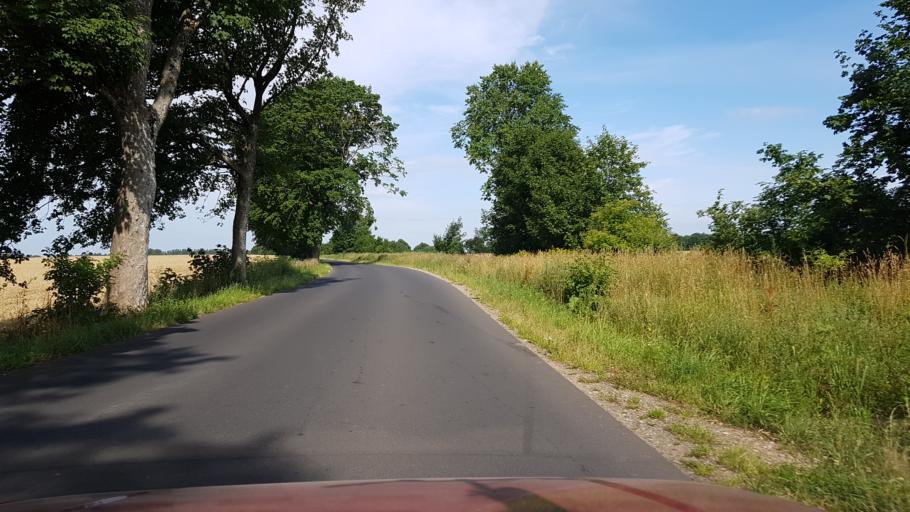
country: PL
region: West Pomeranian Voivodeship
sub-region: Powiat koszalinski
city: Polanow
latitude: 54.1673
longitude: 16.6076
